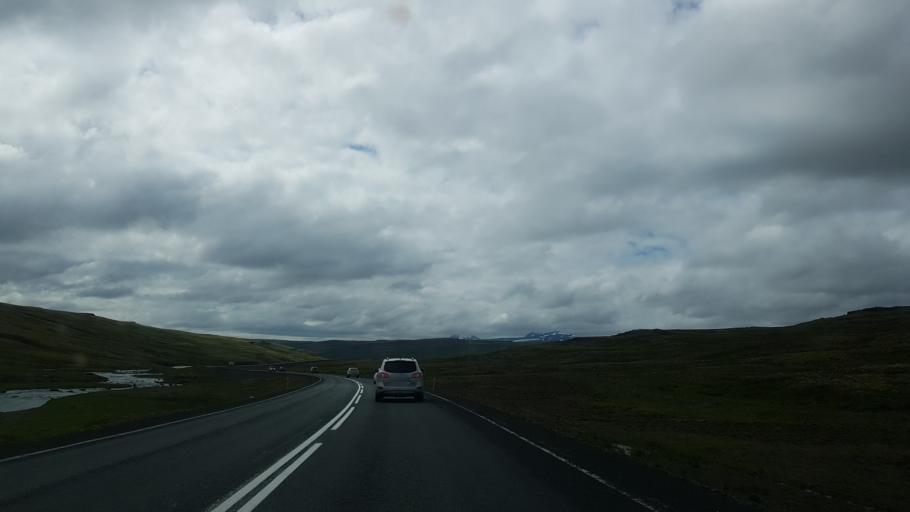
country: IS
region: West
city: Borgarnes
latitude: 64.9167
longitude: -21.1364
